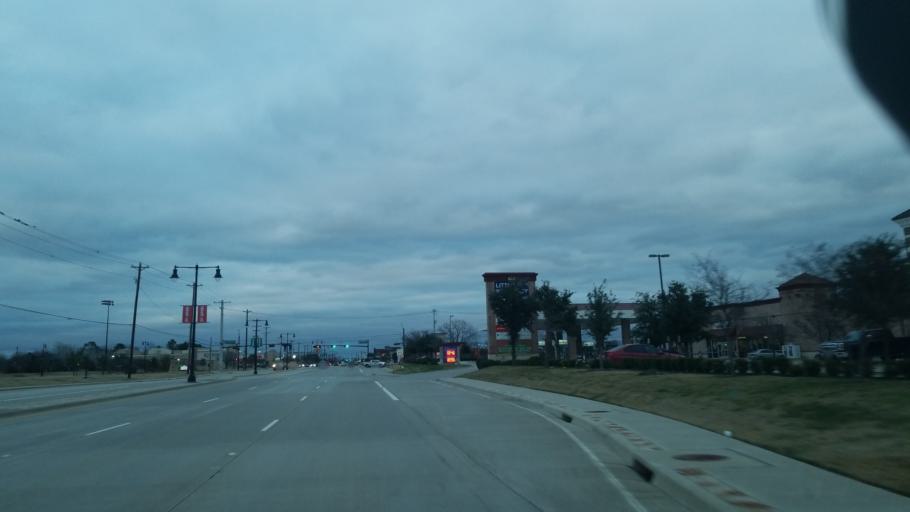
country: US
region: Texas
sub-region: Denton County
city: Little Elm
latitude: 33.1556
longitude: -96.9452
